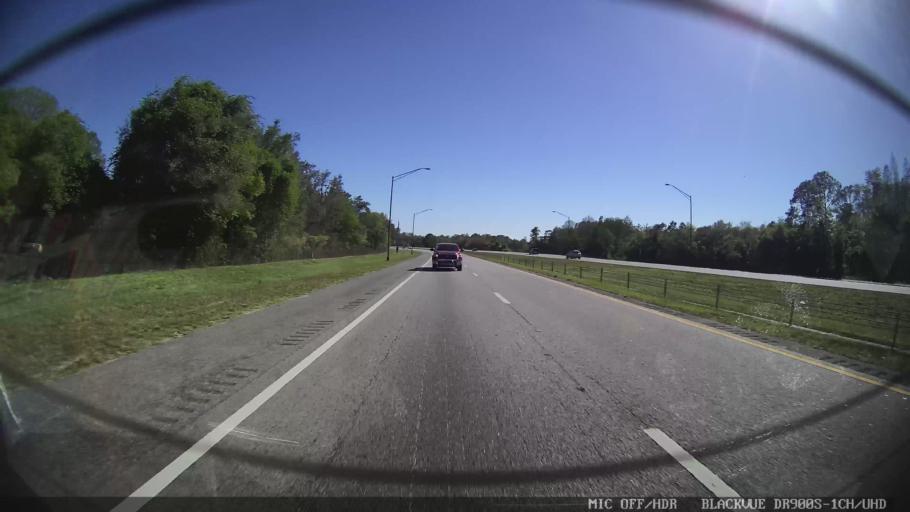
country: US
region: Florida
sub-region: Pasco County
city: Shady Hills
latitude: 28.3279
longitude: -82.5545
